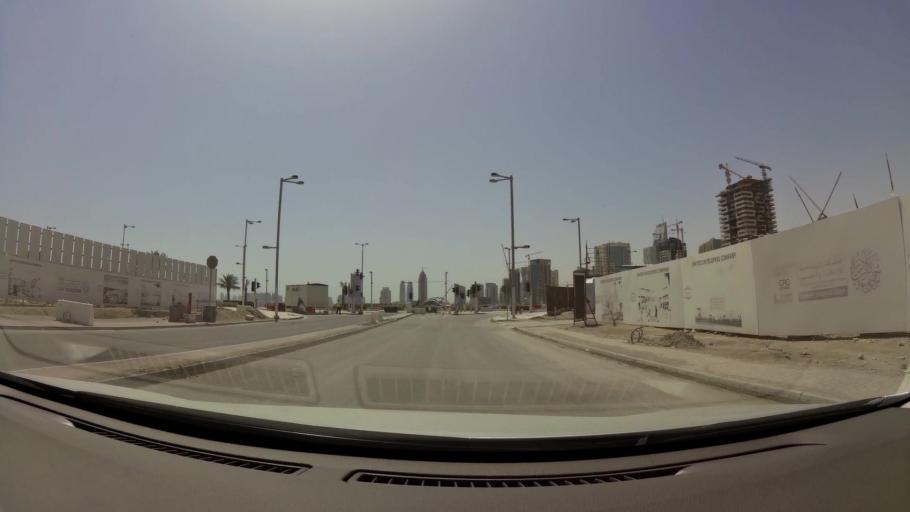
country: QA
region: Baladiyat Umm Salal
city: Umm Salal Muhammad
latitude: 25.4014
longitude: 51.5226
